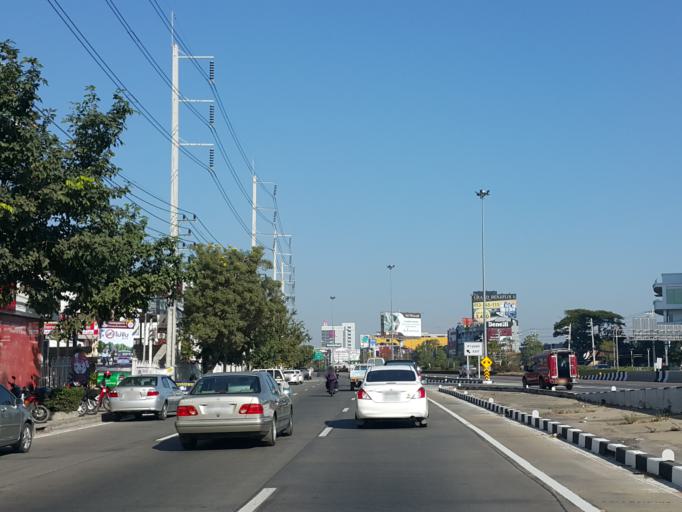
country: TH
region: Chiang Mai
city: Chiang Mai
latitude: 18.7866
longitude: 99.0260
